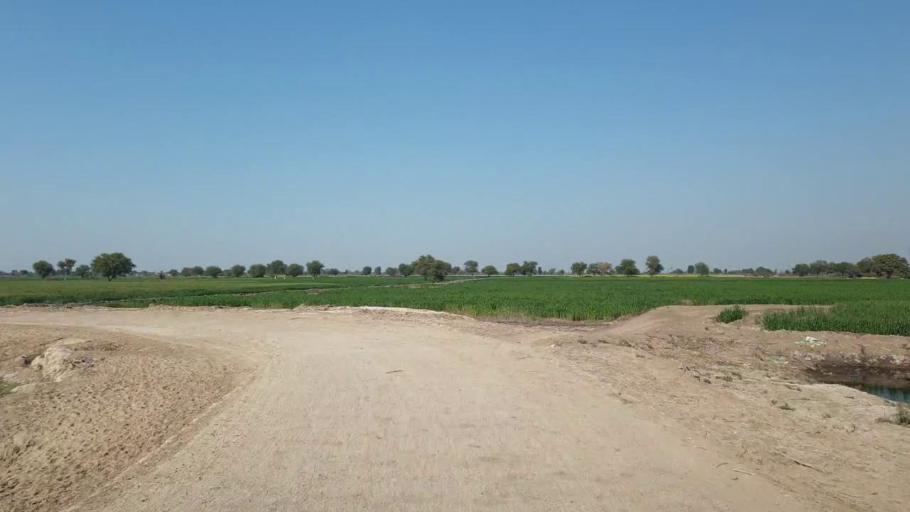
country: PK
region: Sindh
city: Shahdadpur
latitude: 25.9656
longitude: 68.6420
